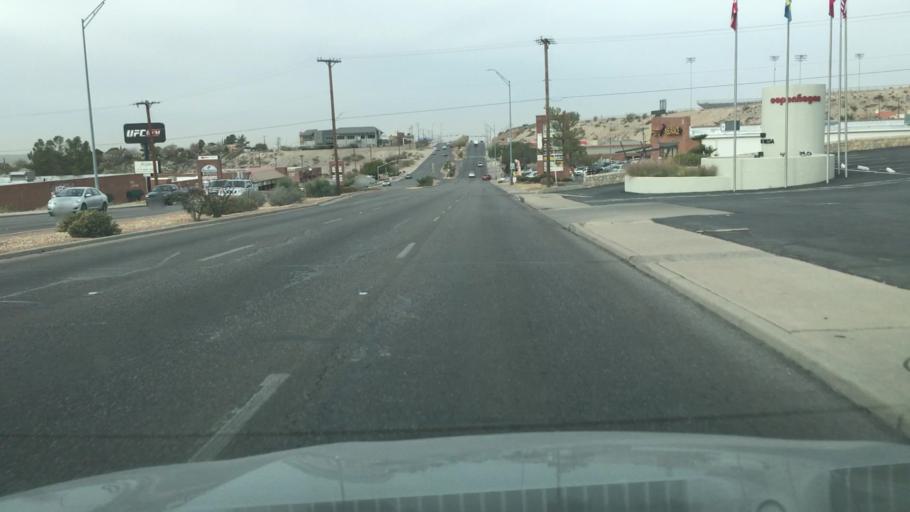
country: US
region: New Mexico
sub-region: Dona Ana County
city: Sunland Park
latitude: 31.8337
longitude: -106.5396
